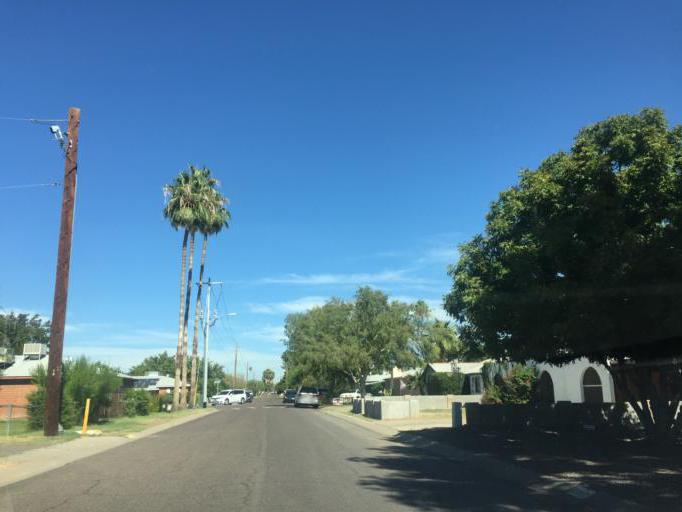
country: US
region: Arizona
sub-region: Maricopa County
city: Phoenix
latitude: 33.5349
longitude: -112.0606
